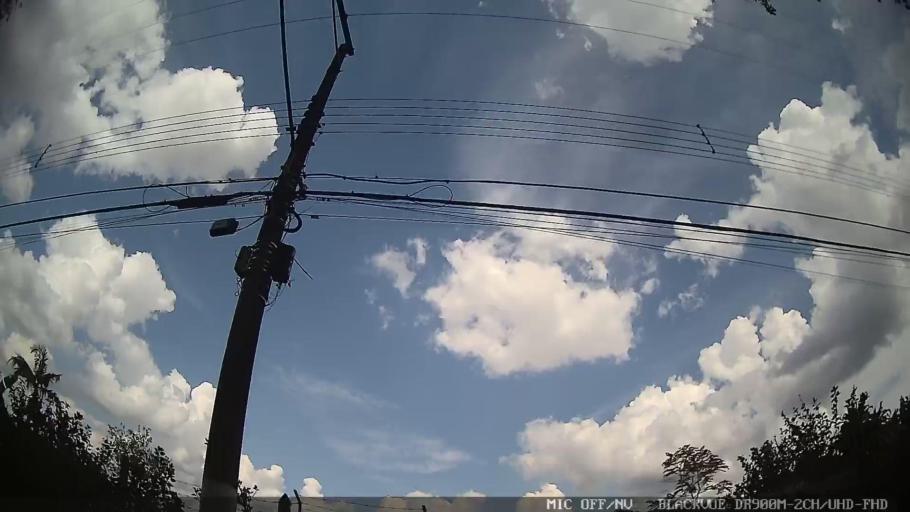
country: BR
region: Sao Paulo
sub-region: Braganca Paulista
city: Braganca Paulista
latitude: -22.9787
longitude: -46.5547
